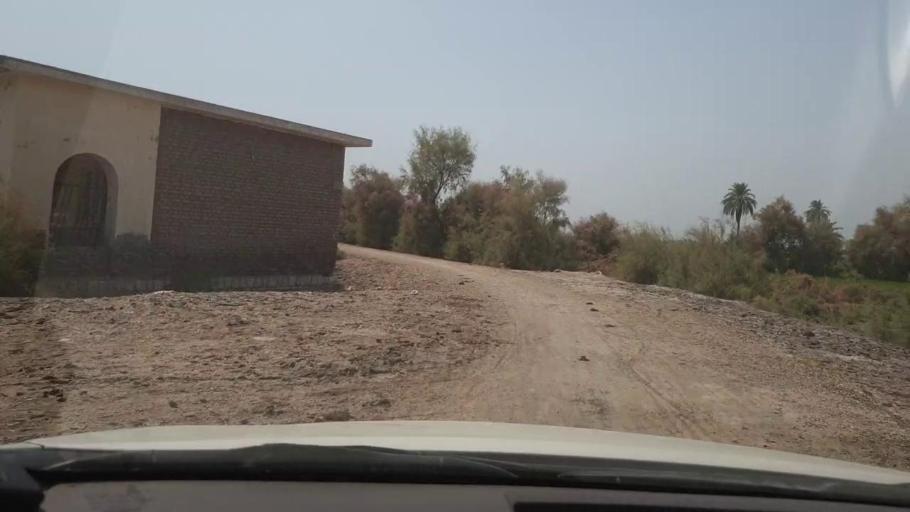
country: PK
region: Sindh
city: Shikarpur
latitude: 27.9194
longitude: 68.6007
